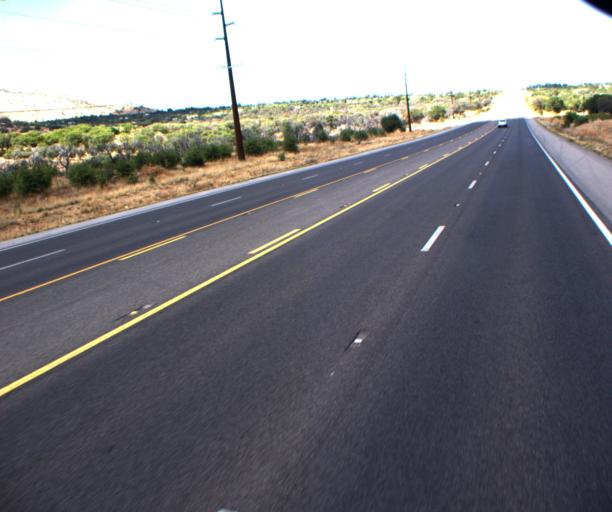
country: US
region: Arizona
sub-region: Cochise County
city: Sierra Vista Southeast
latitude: 31.4124
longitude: -110.2407
